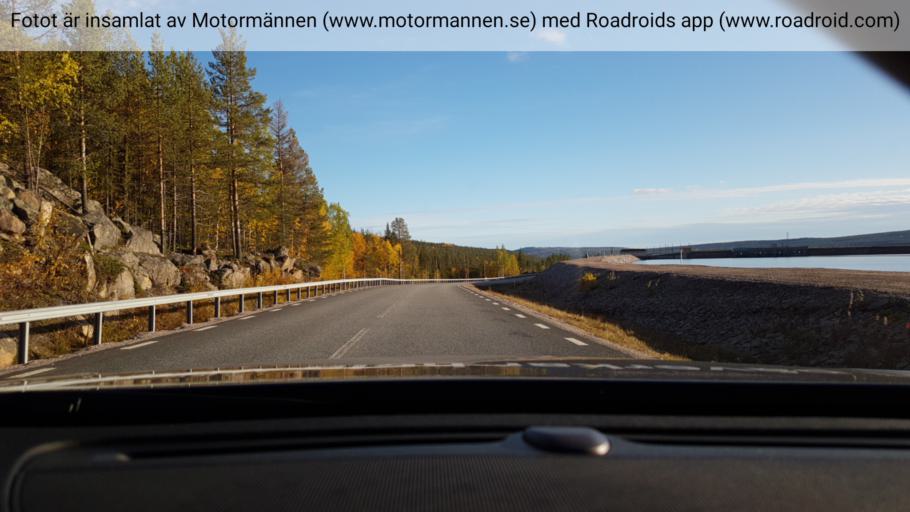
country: SE
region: Norrbotten
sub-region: Jokkmokks Kommun
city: Jokkmokk
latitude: 66.8914
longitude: 19.8280
